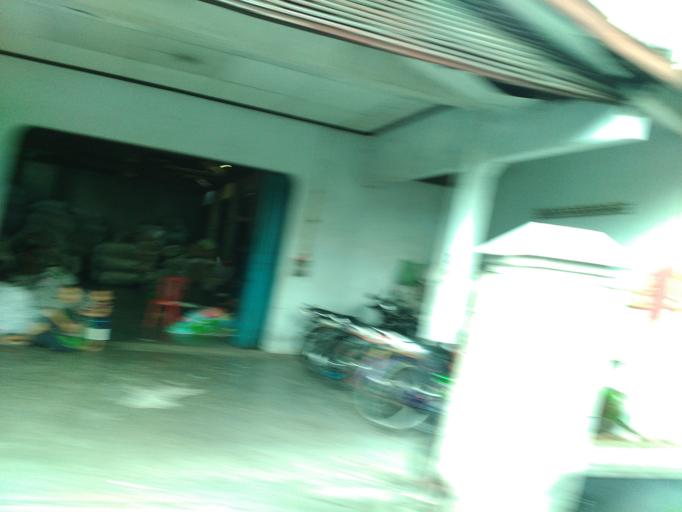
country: ID
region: Central Java
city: Ceper
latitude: -7.6781
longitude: 110.6504
